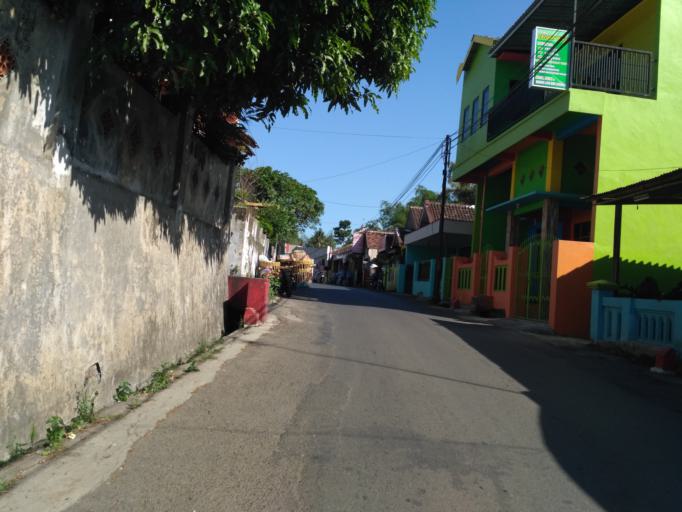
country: ID
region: East Java
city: Singosari
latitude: -7.9158
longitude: 112.6614
